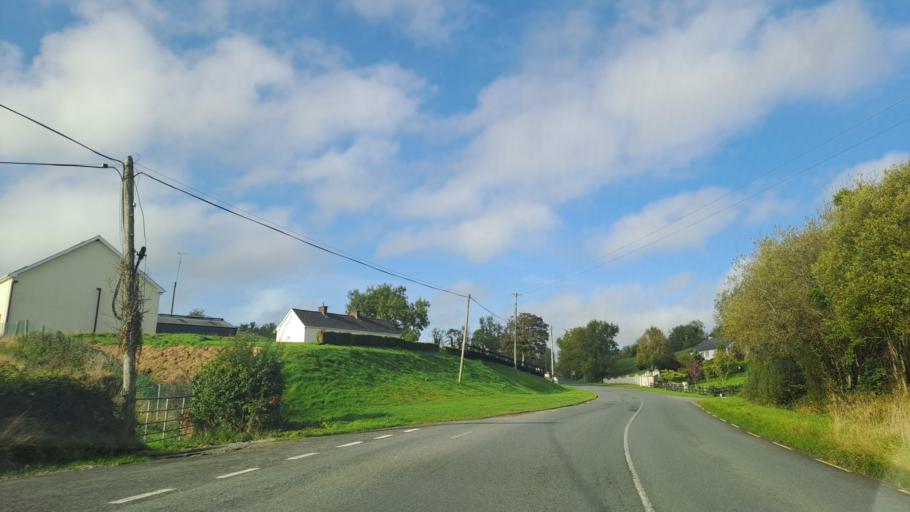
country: IE
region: Ulster
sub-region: An Cabhan
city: Cootehill
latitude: 54.0444
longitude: -6.9969
